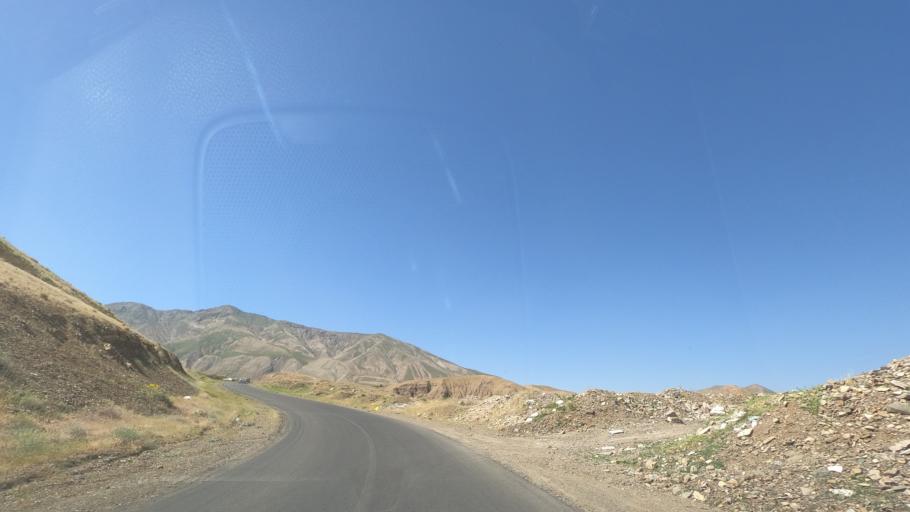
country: IR
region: Alborz
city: Karaj
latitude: 35.9398
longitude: 51.0792
